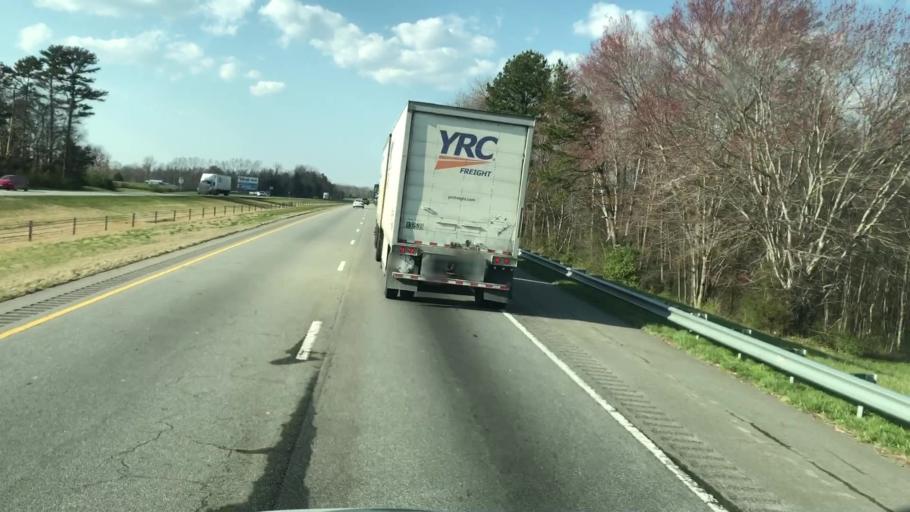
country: US
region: North Carolina
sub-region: Yadkin County
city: Yadkinville
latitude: 36.0405
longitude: -80.8199
